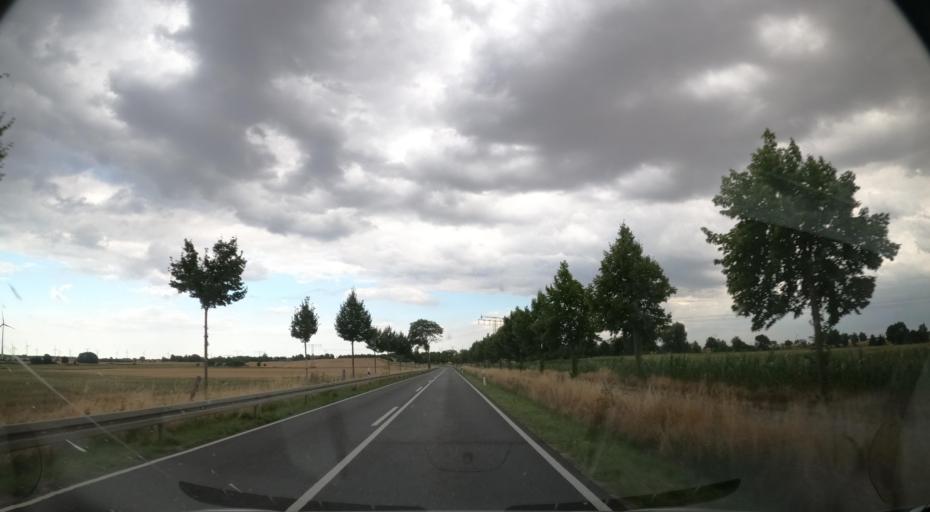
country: DE
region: Mecklenburg-Vorpommern
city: Strasburg
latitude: 53.4945
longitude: 13.7913
